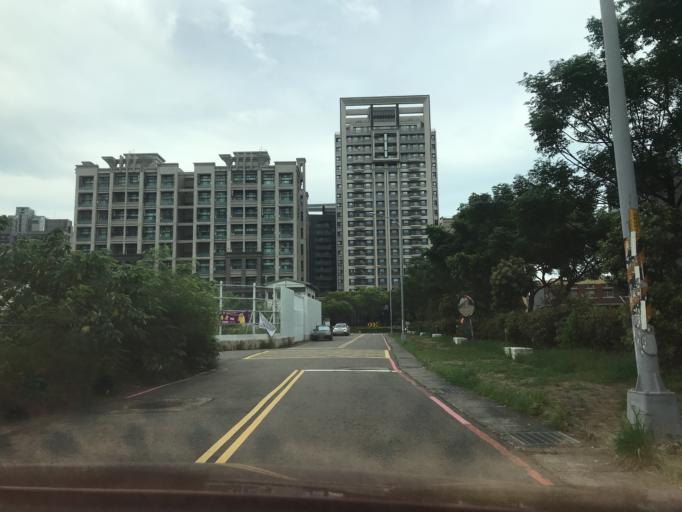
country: TW
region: Taiwan
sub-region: Hsinchu
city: Zhubei
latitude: 24.8149
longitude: 121.0343
